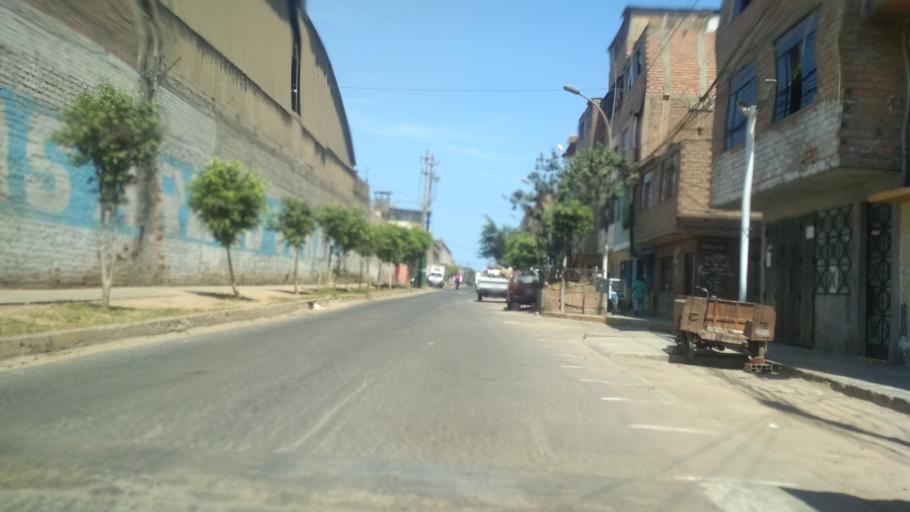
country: PE
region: Callao
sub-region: Callao
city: Callao
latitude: -12.0429
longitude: -77.0858
